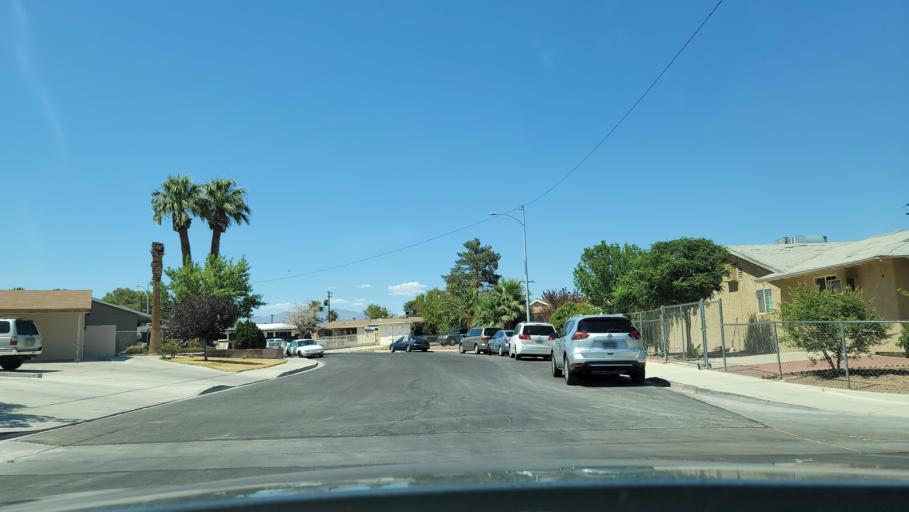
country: US
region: Nevada
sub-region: Clark County
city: Las Vegas
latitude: 36.1779
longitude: -115.1216
